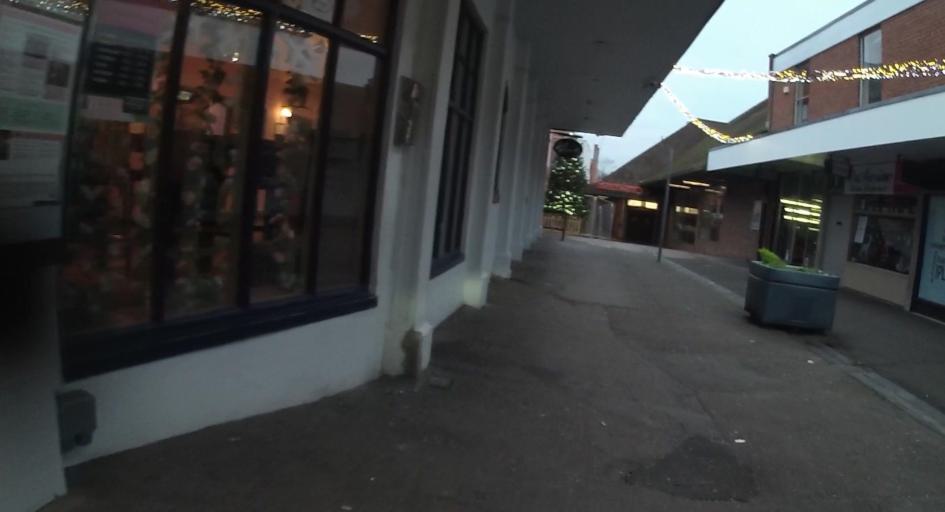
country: GB
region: England
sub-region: Surrey
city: Farnham
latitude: 51.2158
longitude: -0.7969
